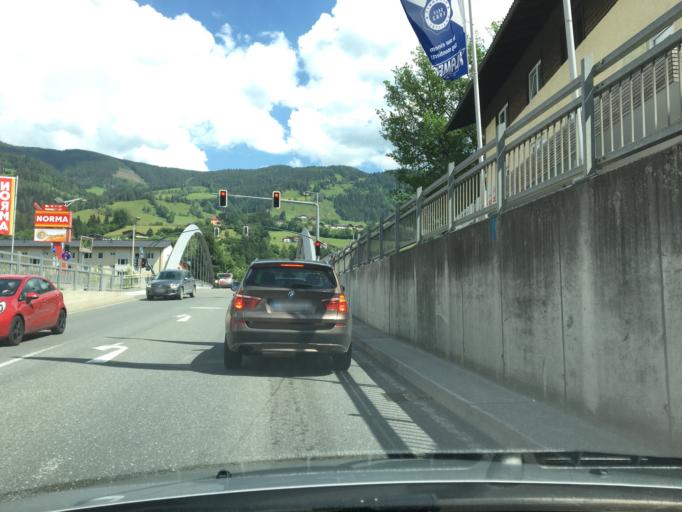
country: AT
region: Salzburg
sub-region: Politischer Bezirk Sankt Johann im Pongau
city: Sankt Johann im Pongau
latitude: 47.3562
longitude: 13.2009
